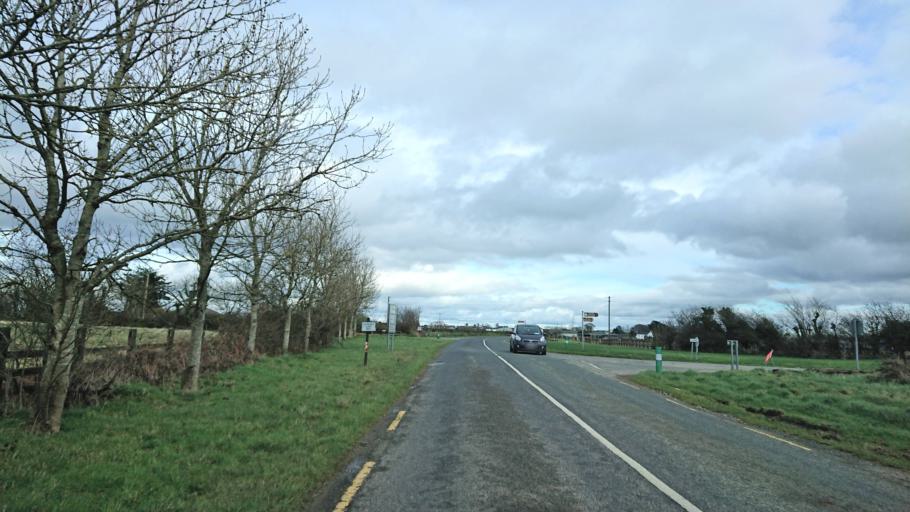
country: IE
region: Munster
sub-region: Waterford
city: Dunmore East
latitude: 52.2441
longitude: -6.9308
